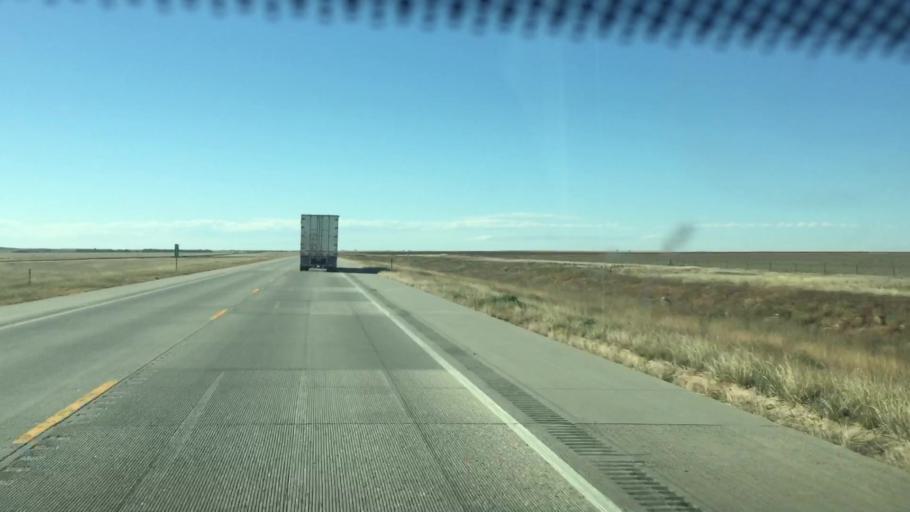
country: US
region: Colorado
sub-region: Kiowa County
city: Eads
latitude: 38.7930
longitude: -102.9396
